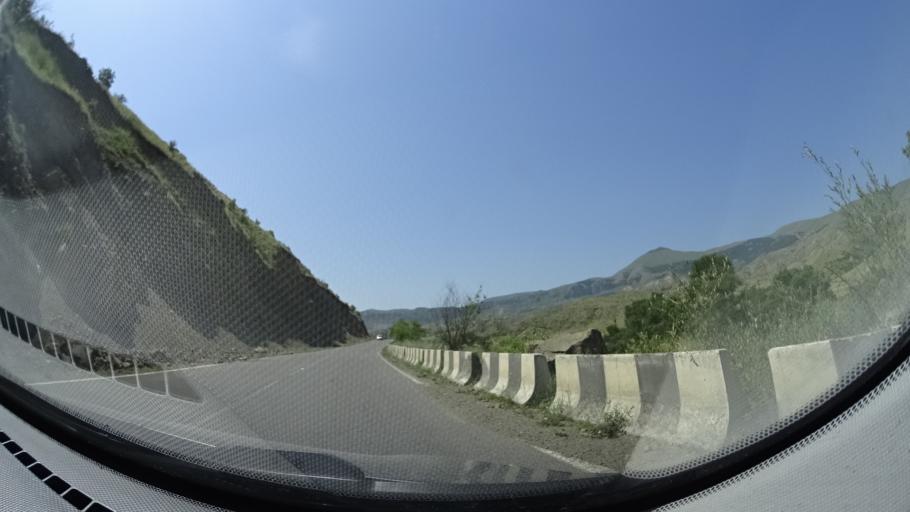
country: GE
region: Samtskhe-Javakheti
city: Aspindza
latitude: 41.5263
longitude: 43.2602
